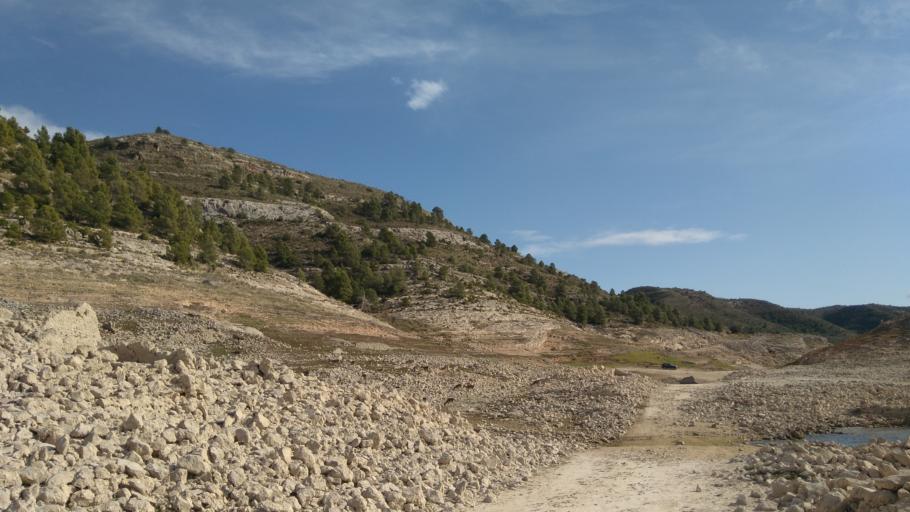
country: ES
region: Valencia
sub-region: Provincia de Valencia
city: Sumacarcer
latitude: 39.1559
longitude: -0.6604
